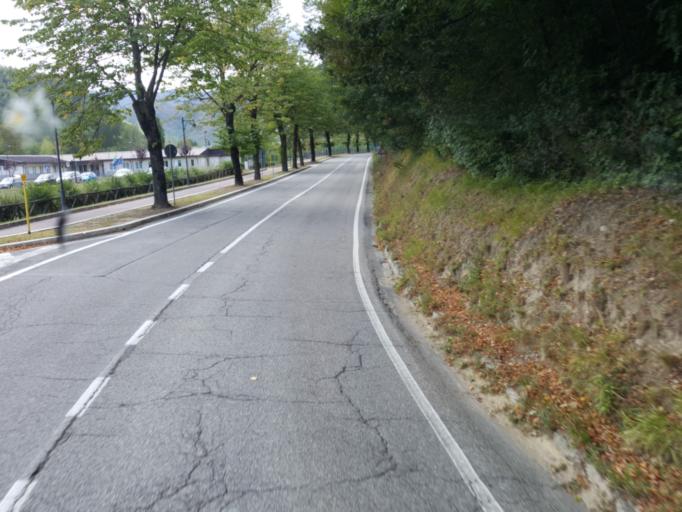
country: IT
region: Emilia-Romagna
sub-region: Forli-Cesena
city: San Piero in Bagno
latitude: 43.8438
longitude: 11.9689
